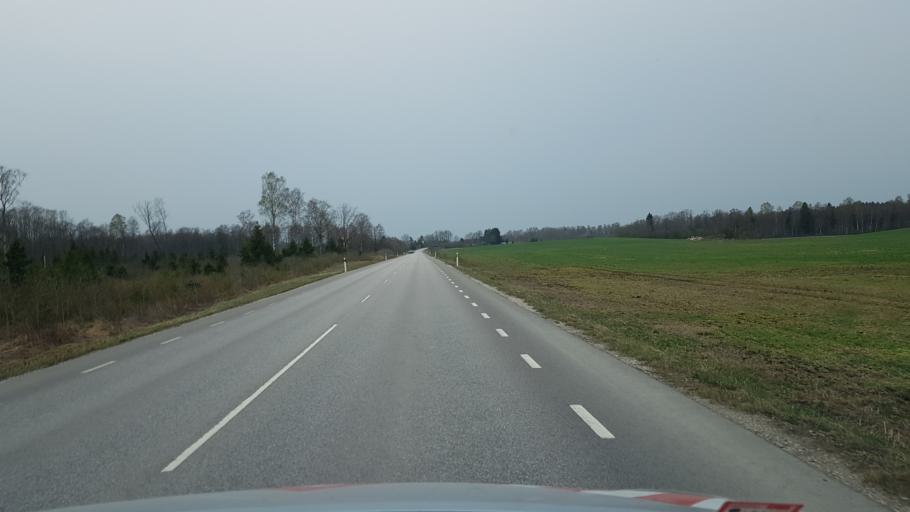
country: EE
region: Harju
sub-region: Raasiku vald
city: Arukula
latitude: 59.3747
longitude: 25.0202
